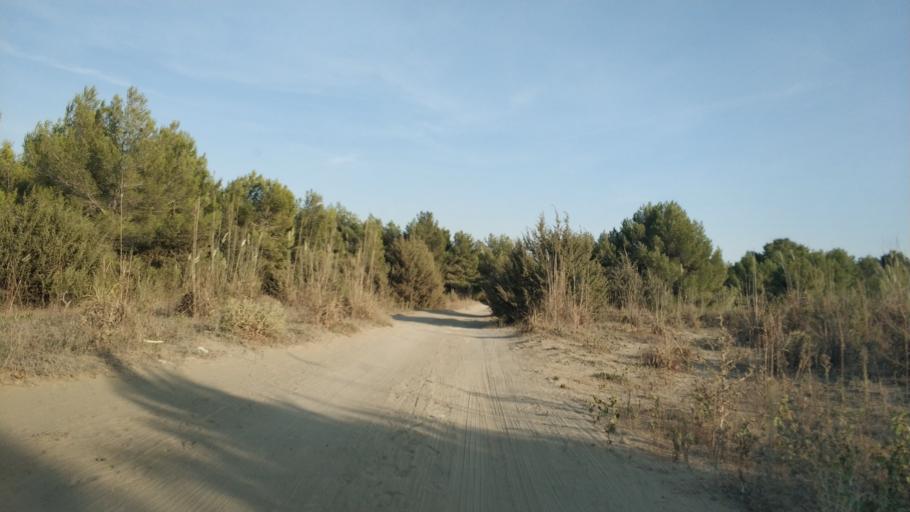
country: AL
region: Fier
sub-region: Rrethi i Lushnjes
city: Divjake
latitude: 40.9540
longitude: 19.4727
